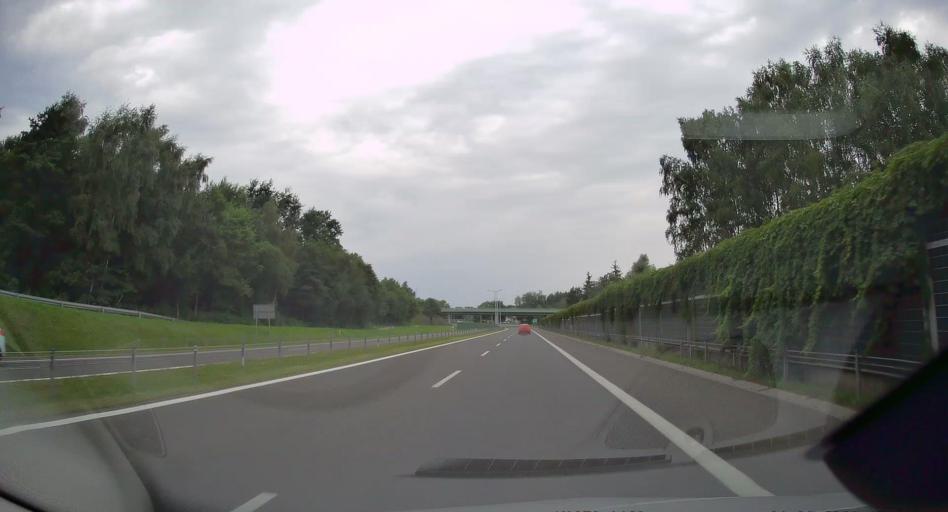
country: PL
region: Lesser Poland Voivodeship
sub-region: Powiat tarnowski
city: Koszyce Wielkie
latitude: 49.9900
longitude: 20.9405
